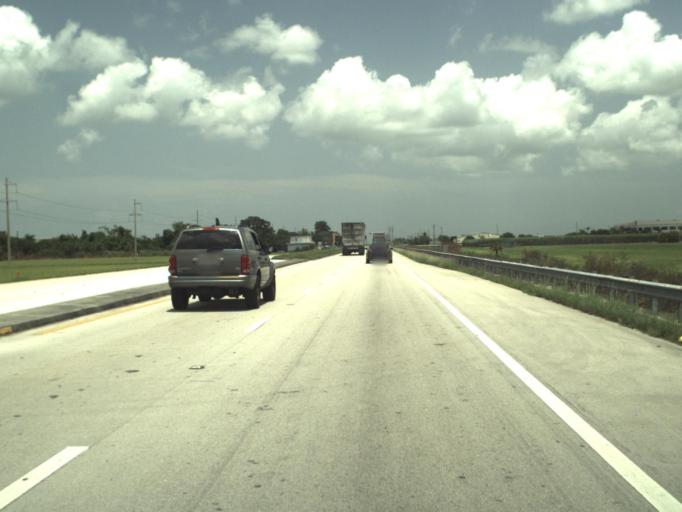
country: US
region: Florida
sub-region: Palm Beach County
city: Belle Glade
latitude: 26.7005
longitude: -80.6679
